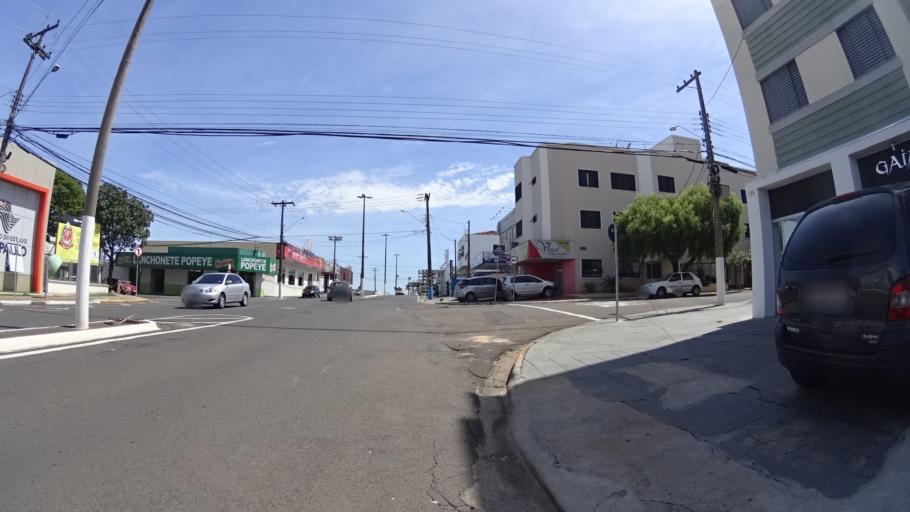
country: BR
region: Sao Paulo
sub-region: Marilia
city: Marilia
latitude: -22.2271
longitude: -49.9348
